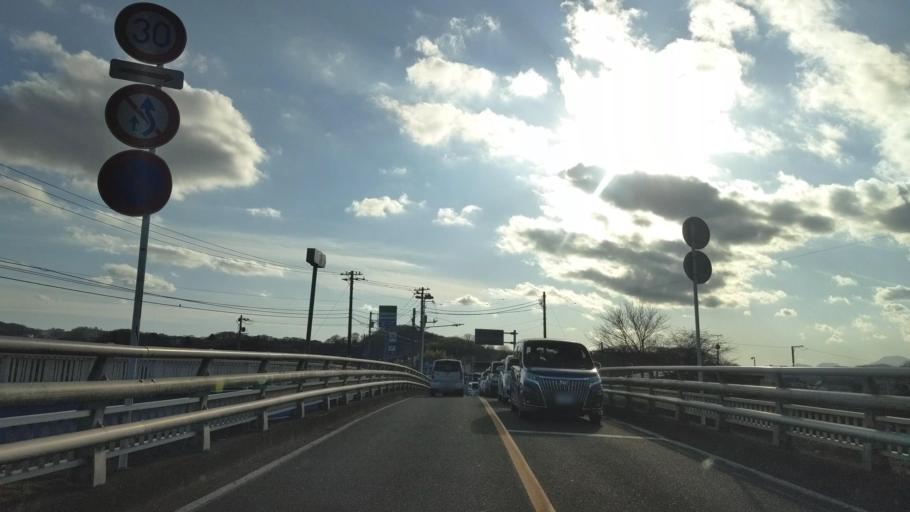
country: JP
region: Kanagawa
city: Hadano
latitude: 35.3561
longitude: 139.2699
